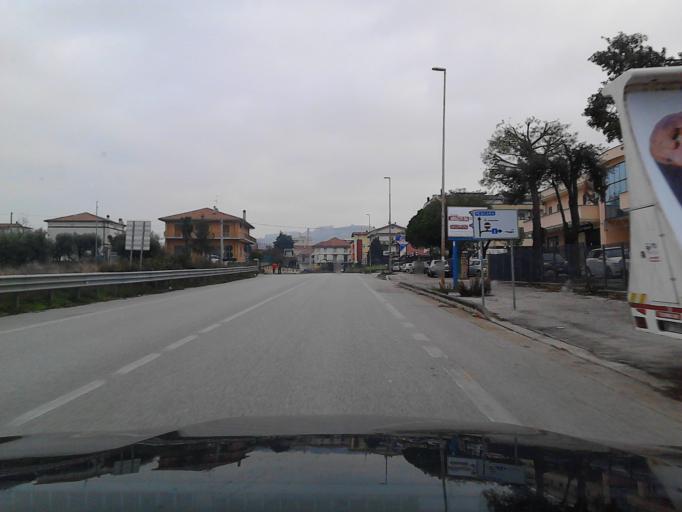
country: IT
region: Abruzzo
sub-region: Provincia di Teramo
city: Alba Adriatica
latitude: 42.8341
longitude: 13.9148
